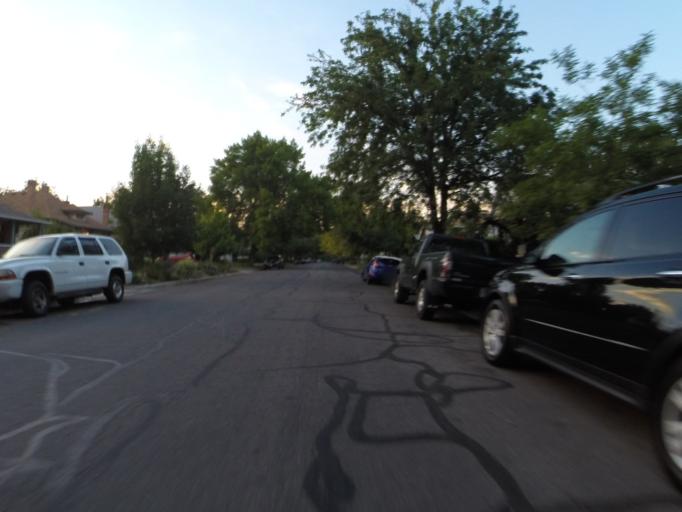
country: US
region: Utah
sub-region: Salt Lake County
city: Salt Lake City
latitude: 40.7420
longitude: -111.8682
